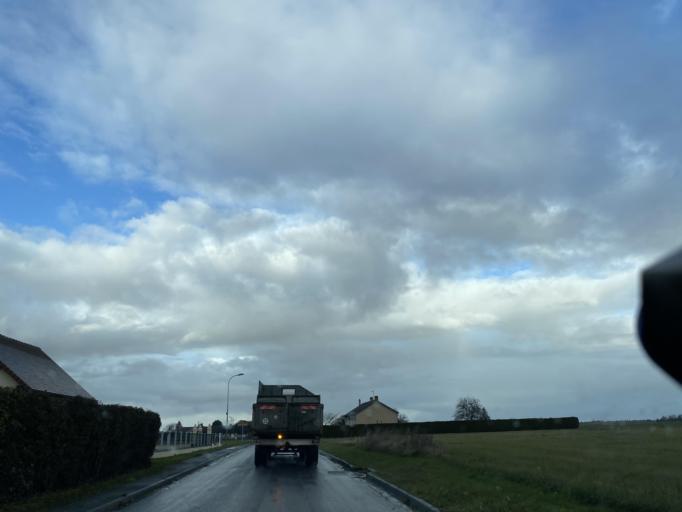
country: FR
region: Haute-Normandie
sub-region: Departement de l'Eure
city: Damville
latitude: 48.8159
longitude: 1.0612
